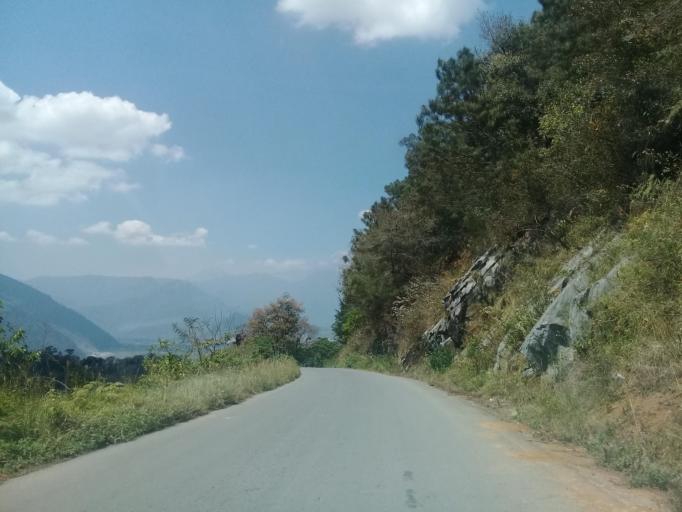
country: MX
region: Veracruz
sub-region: Tlilapan
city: Tonalixco
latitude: 18.7998
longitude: -97.0575
